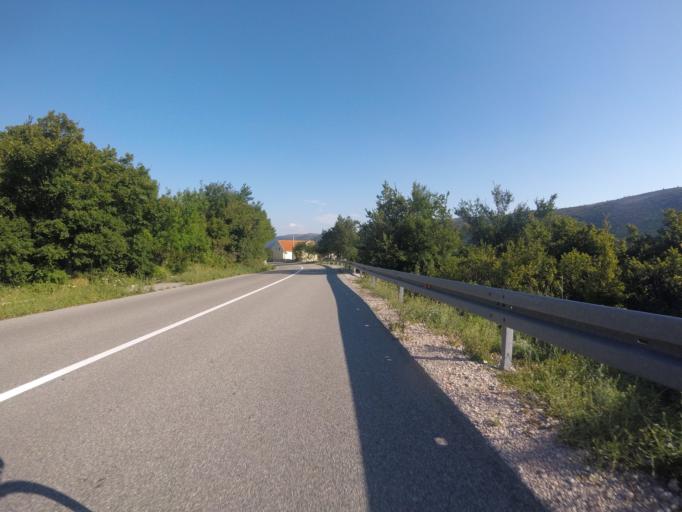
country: HR
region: Primorsko-Goranska
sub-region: Grad Crikvenica
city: Jadranovo
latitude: 45.2451
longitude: 14.6370
